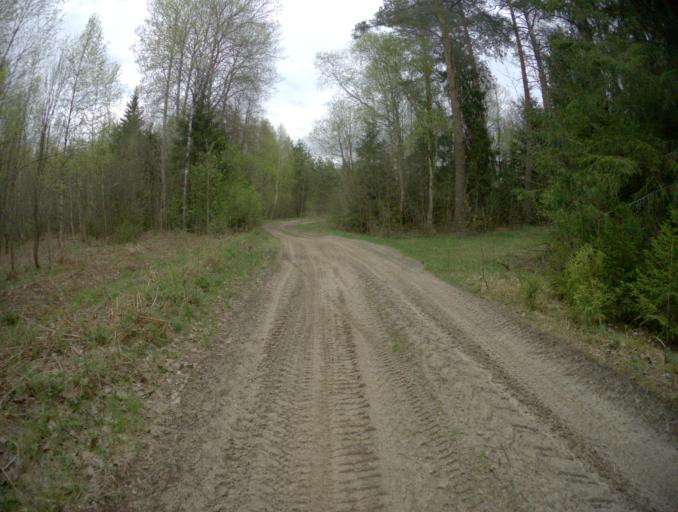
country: RU
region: Vladimir
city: Golovino
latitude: 55.8955
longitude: 40.4203
